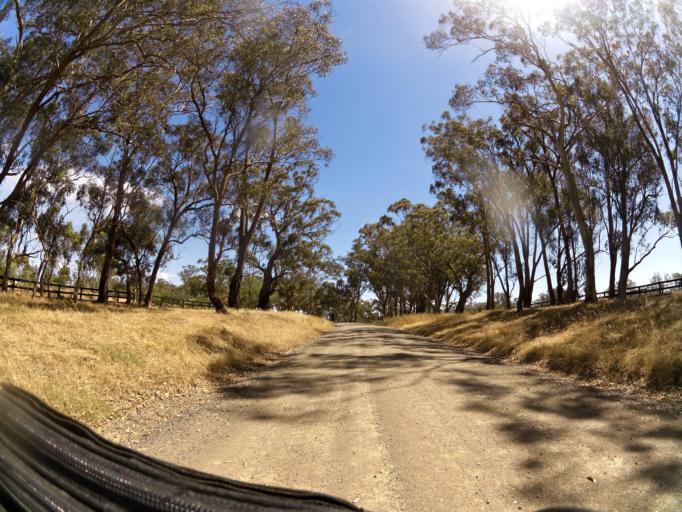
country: AU
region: Victoria
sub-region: Campaspe
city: Kyabram
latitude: -36.8309
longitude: 145.0751
